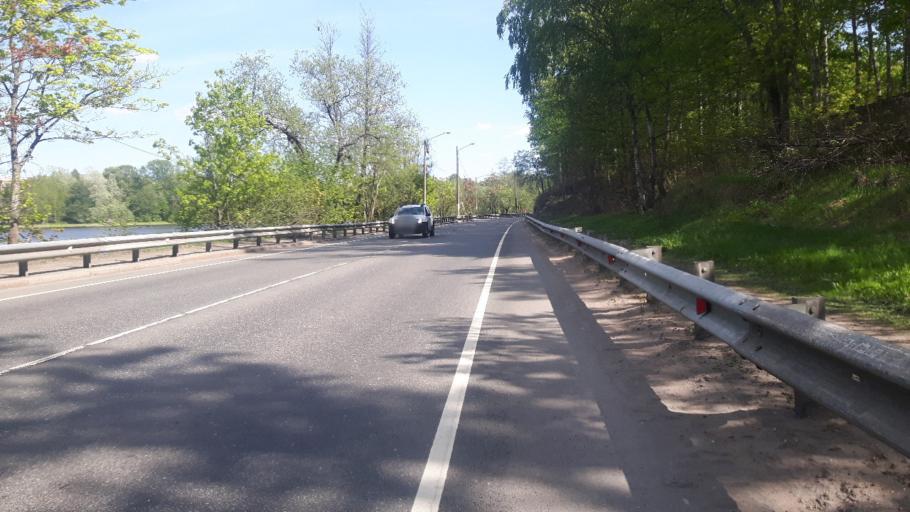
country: RU
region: Leningrad
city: Vyborg
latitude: 60.7243
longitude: 28.7099
